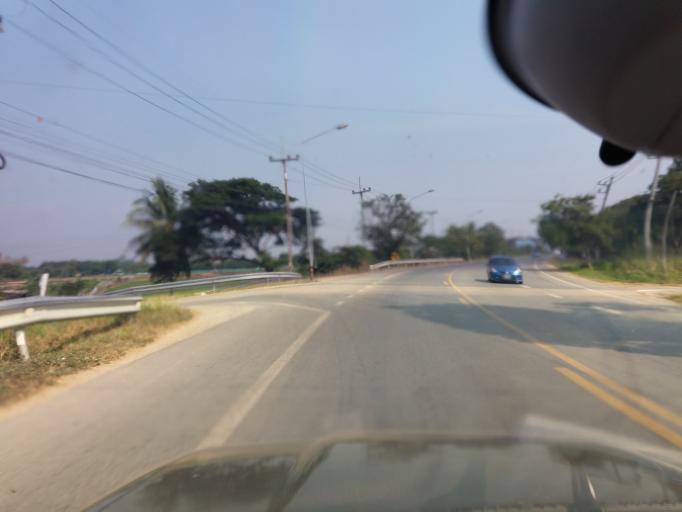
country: TH
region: Sing Buri
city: Sing Buri
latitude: 14.8866
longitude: 100.3718
